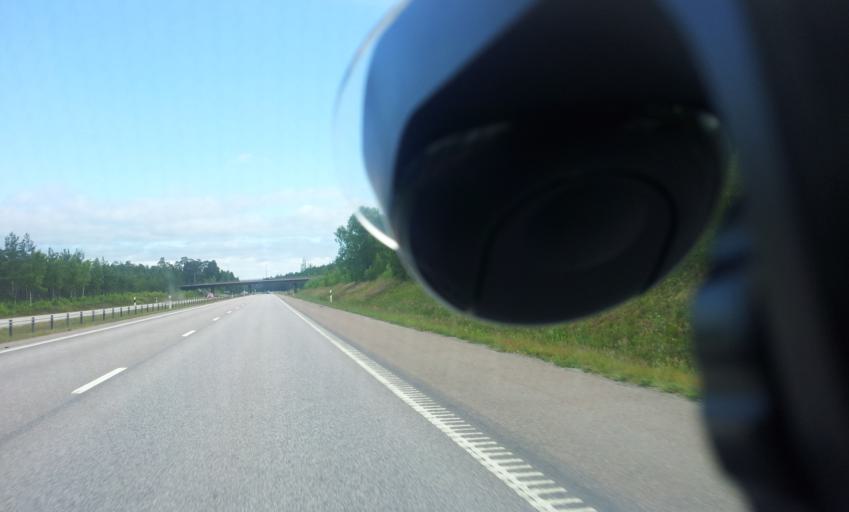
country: SE
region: Kalmar
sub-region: Kalmar Kommun
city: Lindsdal
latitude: 56.7094
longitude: 16.3134
